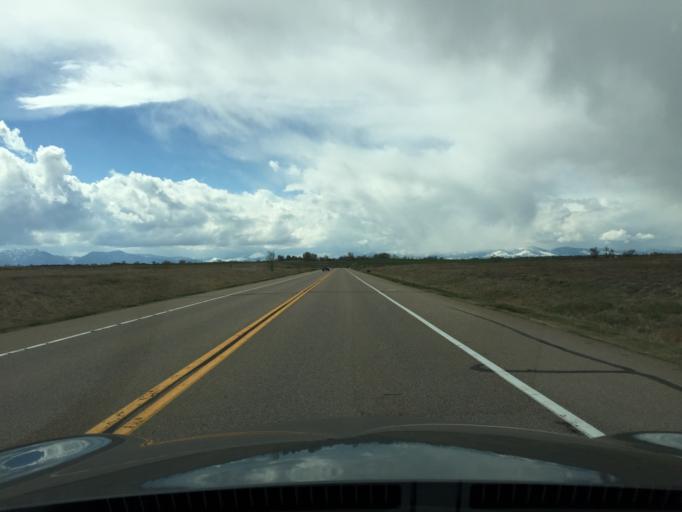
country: US
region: Colorado
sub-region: Boulder County
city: Erie
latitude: 40.0214
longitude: -105.0494
